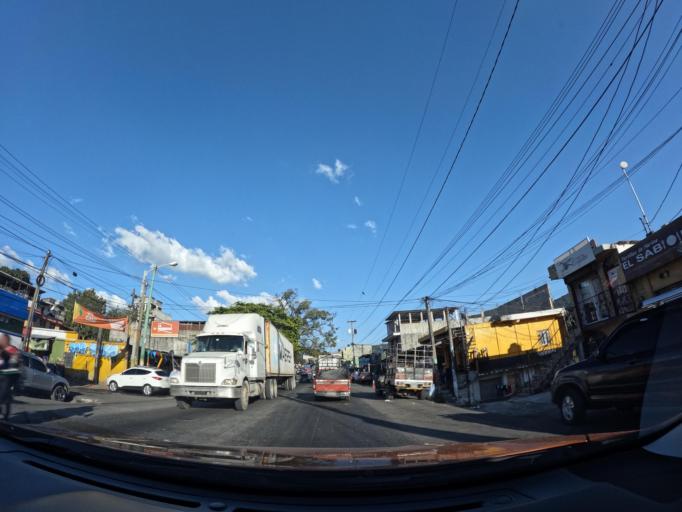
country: GT
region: Escuintla
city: Palin
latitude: 14.4037
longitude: -90.6960
